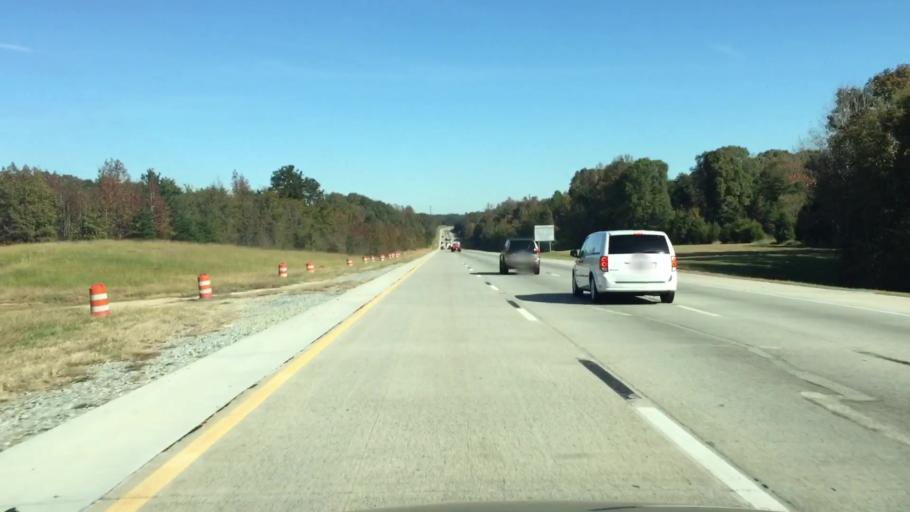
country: US
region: North Carolina
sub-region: Guilford County
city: Jamestown
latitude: 35.9659
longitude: -79.8928
